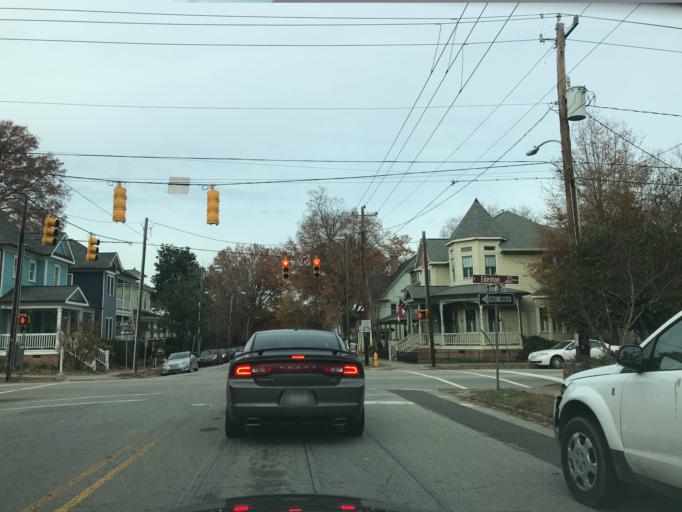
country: US
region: North Carolina
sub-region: Wake County
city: Raleigh
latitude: 35.7808
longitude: -78.6332
